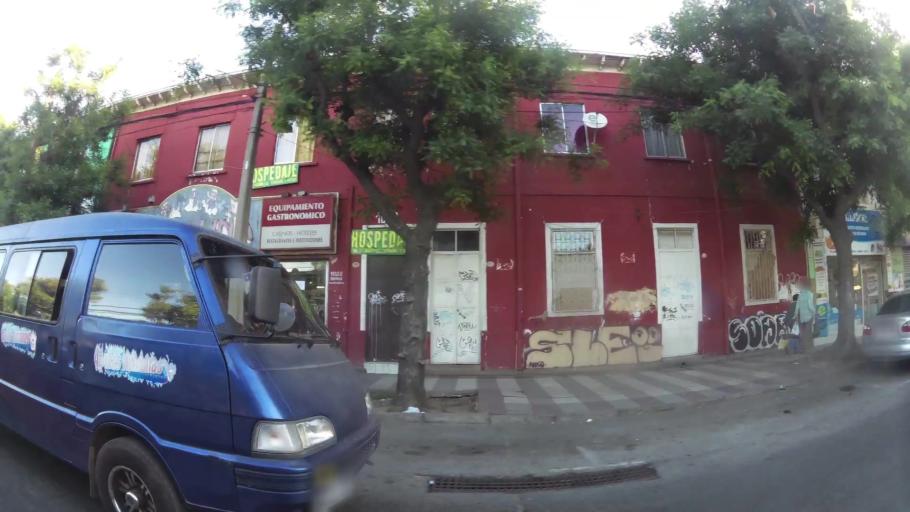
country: CL
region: Valparaiso
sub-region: Provincia de Valparaiso
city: Vina del Mar
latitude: -33.0247
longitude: -71.5471
